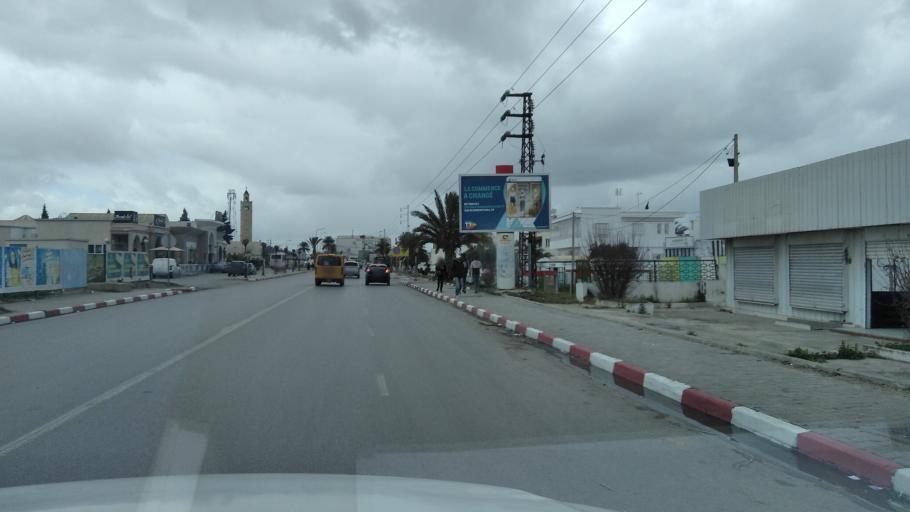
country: TN
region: Bin 'Arus
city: Ben Arous
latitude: 36.7500
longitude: 10.2271
